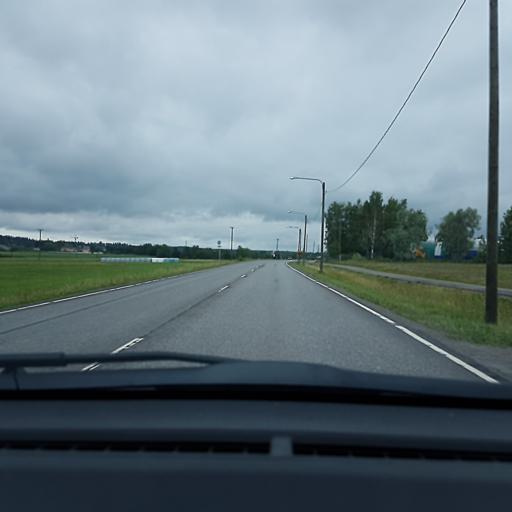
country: FI
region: Uusimaa
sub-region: Helsinki
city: Nickby
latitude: 60.3882
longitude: 25.2850
